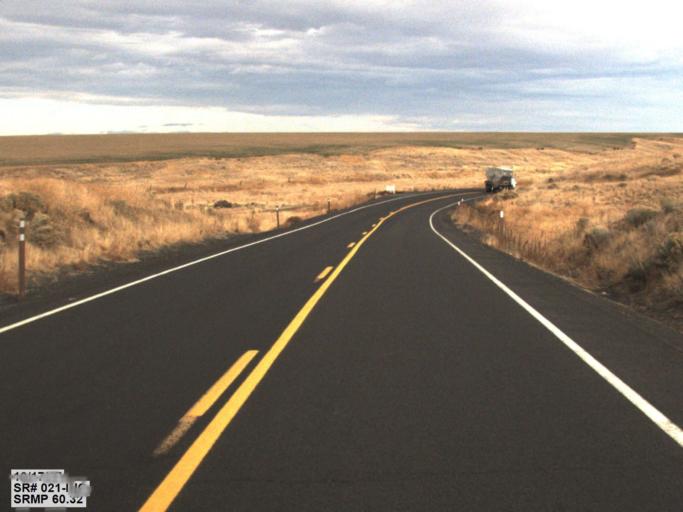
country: US
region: Washington
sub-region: Adams County
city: Ritzville
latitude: 47.3917
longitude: -118.6905
